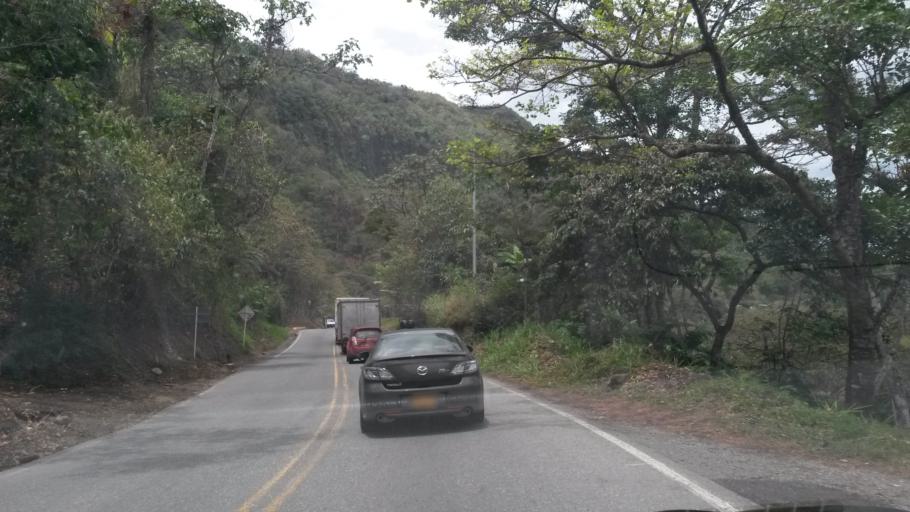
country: CO
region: Cauca
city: Rosas
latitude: 2.2576
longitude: -76.7560
